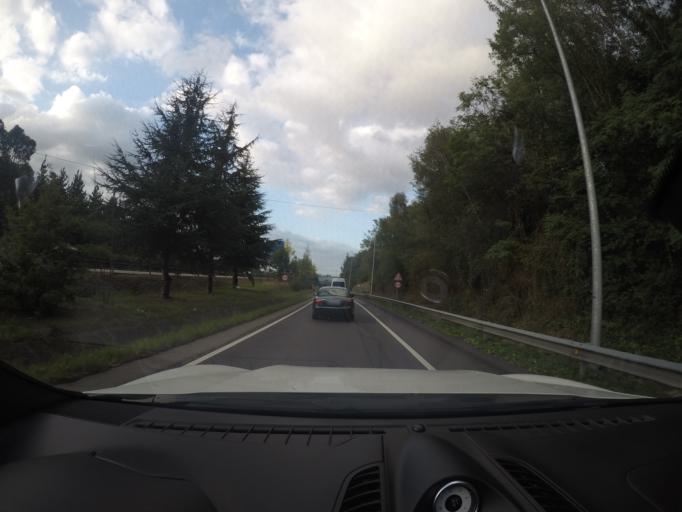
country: ES
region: Asturias
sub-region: Province of Asturias
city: Lugones
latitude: 43.3705
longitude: -5.8123
